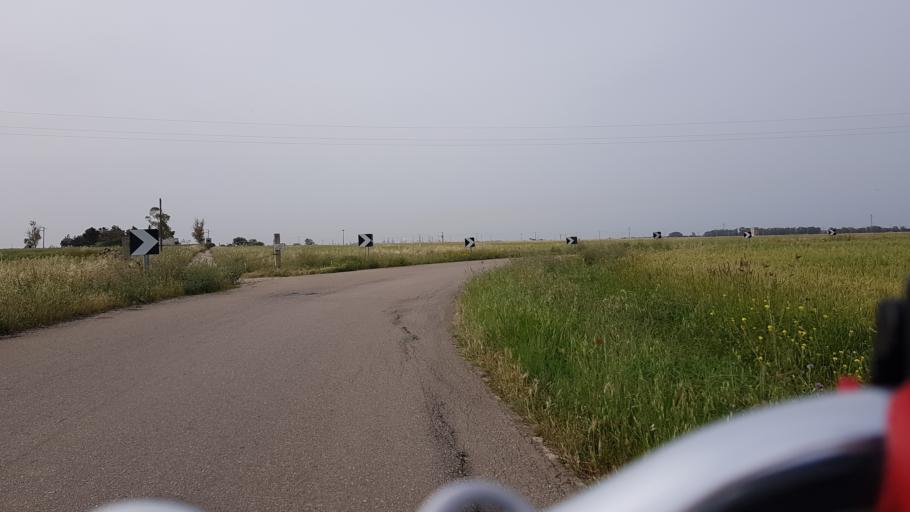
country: IT
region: Apulia
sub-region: Provincia di Brindisi
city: La Rosa
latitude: 40.5740
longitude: 18.0136
